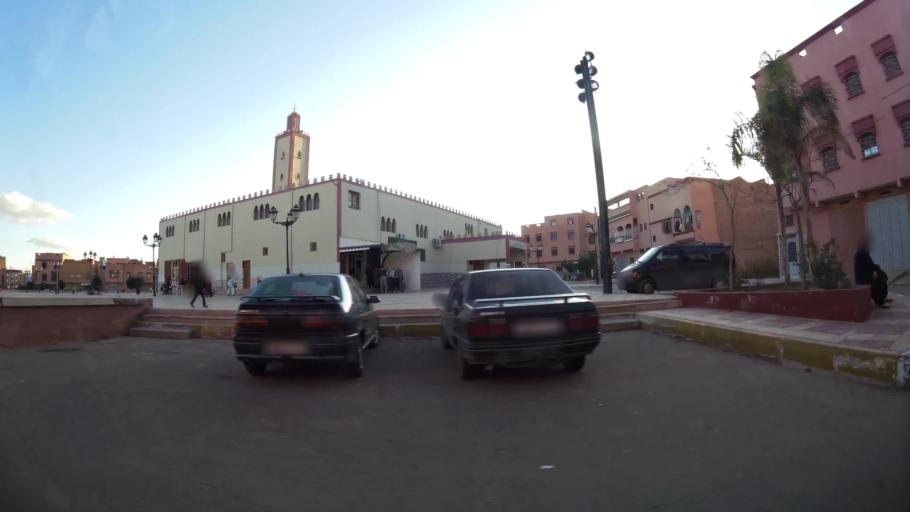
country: MA
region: Marrakech-Tensift-Al Haouz
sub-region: Kelaa-Des-Sraghna
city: Sidi Abdallah
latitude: 32.2376
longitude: -7.9523
